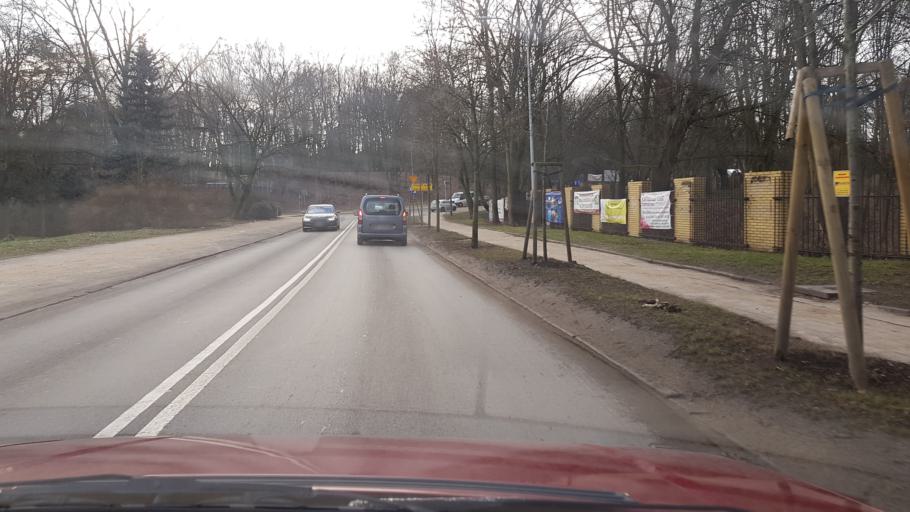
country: PL
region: West Pomeranian Voivodeship
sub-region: Szczecin
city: Szczecin
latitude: 53.4475
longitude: 14.5275
